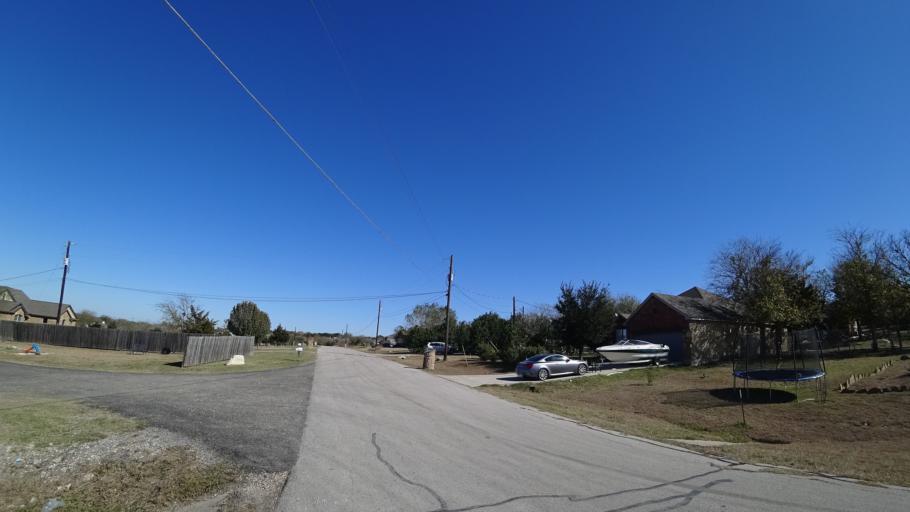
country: US
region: Texas
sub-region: Travis County
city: Garfield
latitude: 30.1013
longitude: -97.6013
